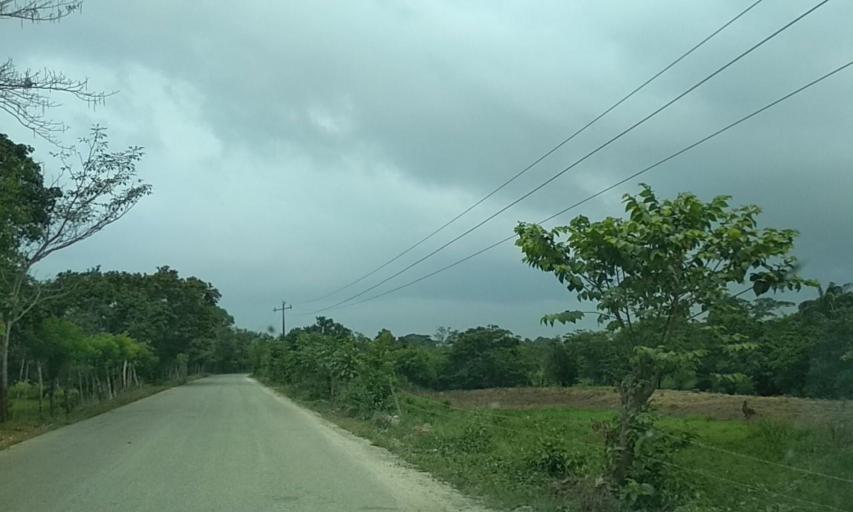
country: MX
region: Tabasco
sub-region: Huimanguillo
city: Francisco Rueda
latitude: 17.5955
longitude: -94.0899
